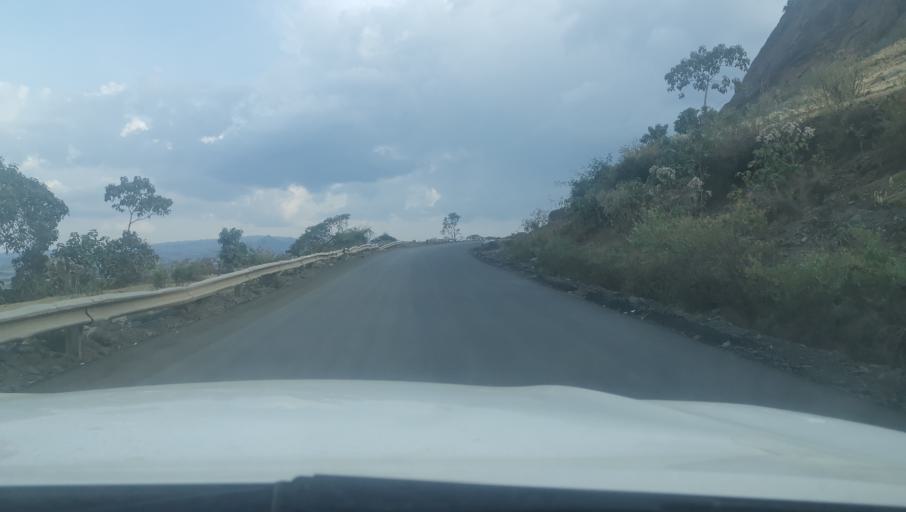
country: ET
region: Oromiya
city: Guder
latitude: 8.9750
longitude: 37.7494
